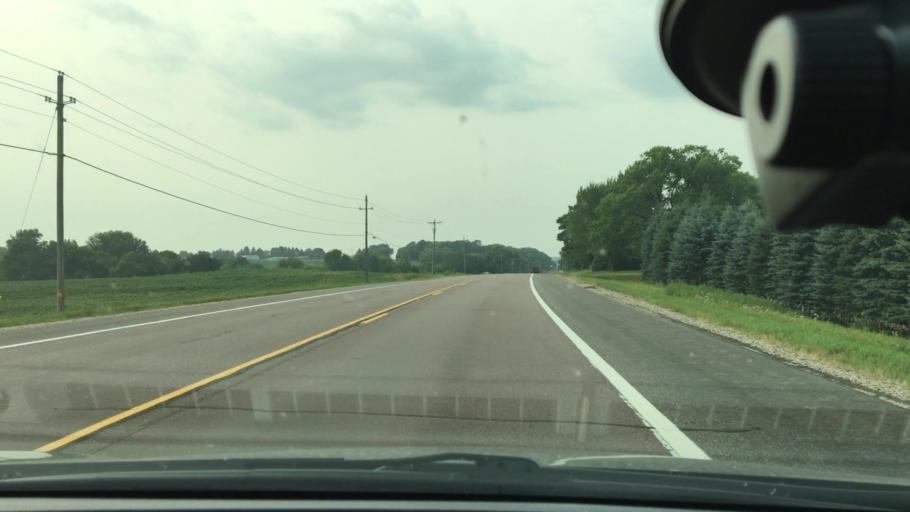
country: US
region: Minnesota
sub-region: Hennepin County
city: Dayton
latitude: 45.2462
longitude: -93.5315
